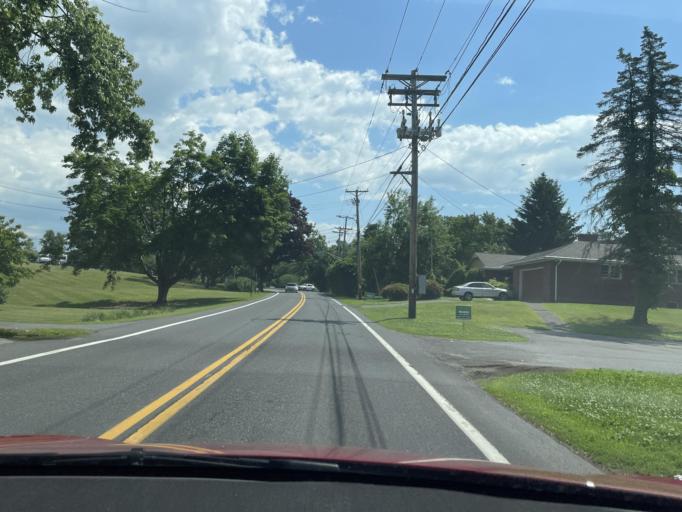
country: US
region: New York
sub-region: Ulster County
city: Lincoln Park
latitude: 41.9399
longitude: -73.9897
